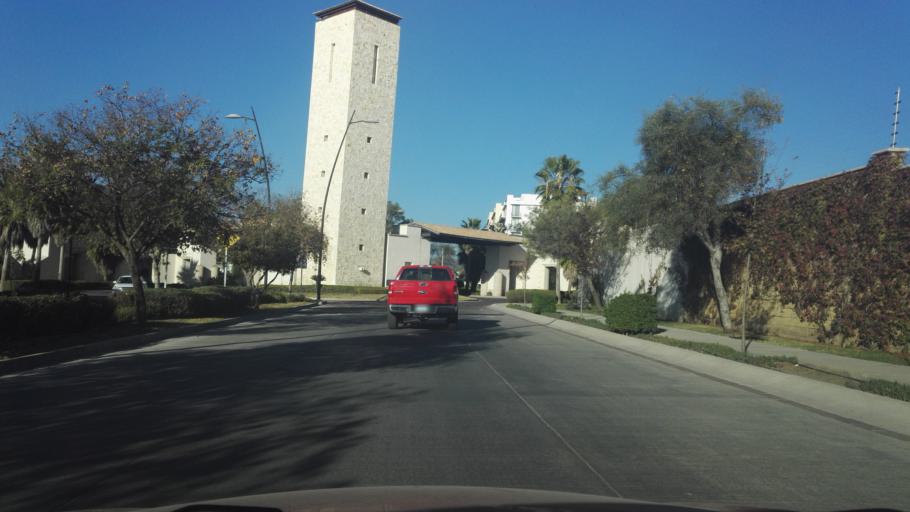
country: MX
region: Guanajuato
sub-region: Leon
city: Ladrilleras del Refugio
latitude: 21.0662
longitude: -101.5971
